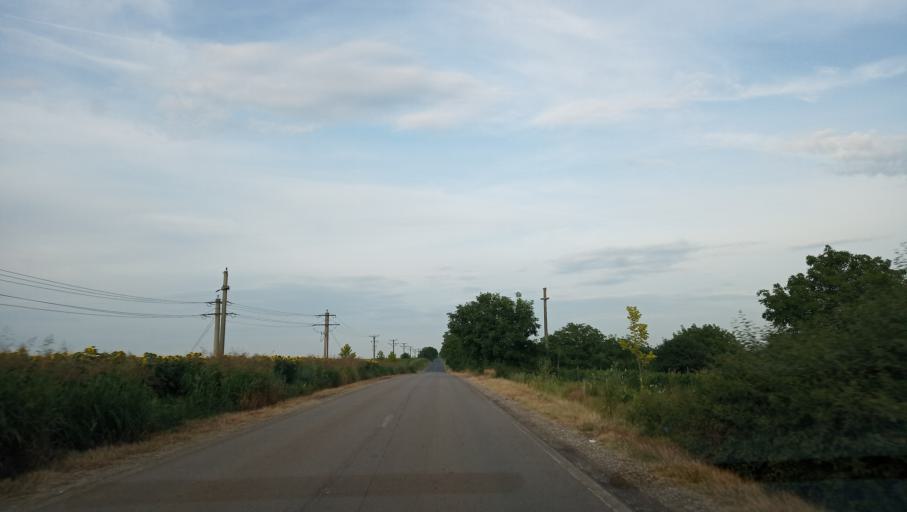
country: RO
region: Giurgiu
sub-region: Comuna Prundu
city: Prundu
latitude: 44.0986
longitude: 26.2542
